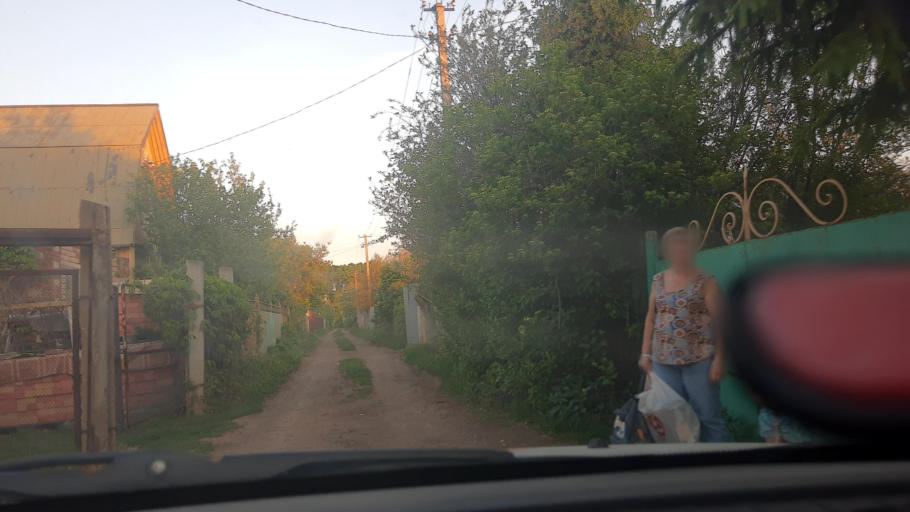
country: RU
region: Bashkortostan
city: Ufa
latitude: 54.5516
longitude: 55.9289
